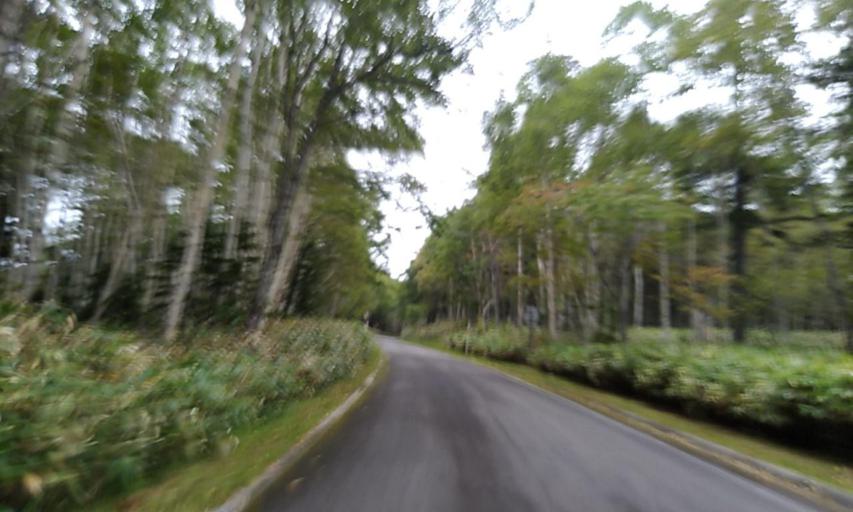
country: JP
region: Hokkaido
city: Bihoro
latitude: 43.5687
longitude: 144.2207
